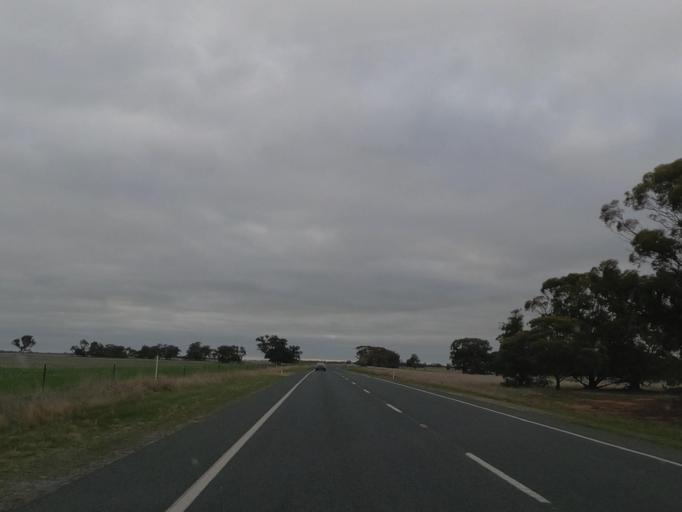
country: AU
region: Victoria
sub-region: Greater Bendigo
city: Long Gully
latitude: -36.2423
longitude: 143.9591
